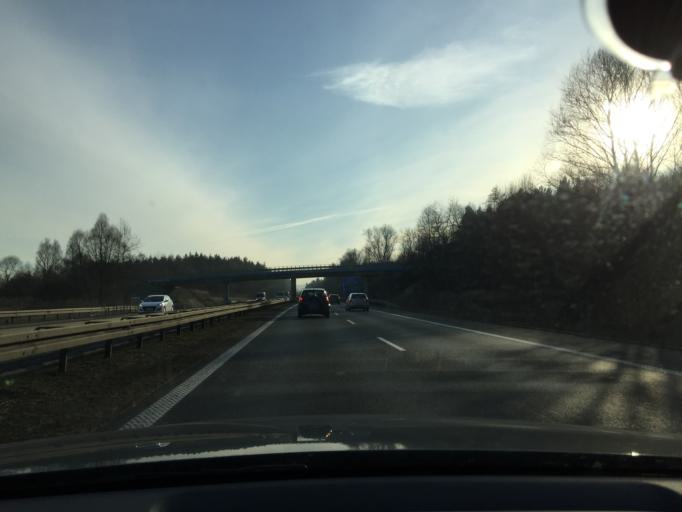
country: PL
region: Lesser Poland Voivodeship
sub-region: Krakow
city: Sidzina
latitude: 50.0076
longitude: 19.8506
